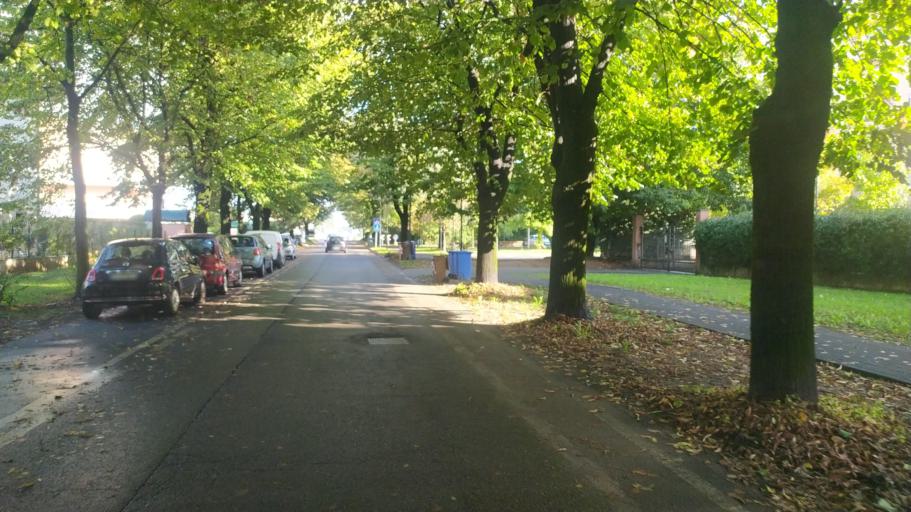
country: IT
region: Lombardy
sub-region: Citta metropolitana di Milano
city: Cernusco sul Naviglio
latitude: 45.5311
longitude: 9.3374
